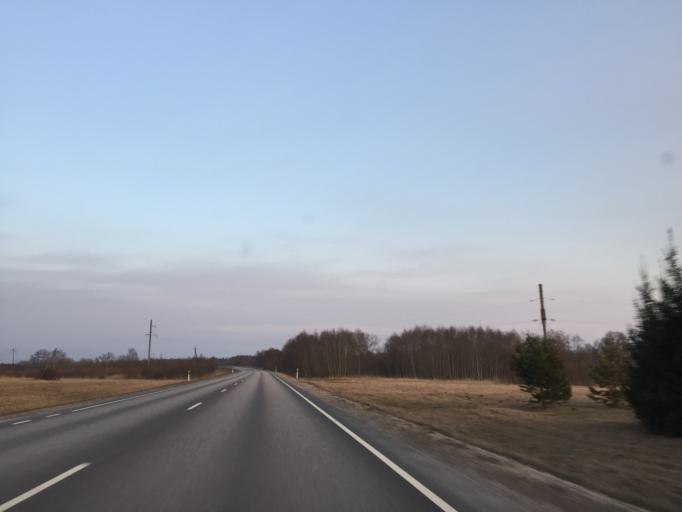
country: EE
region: Paernumaa
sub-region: Audru vald
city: Audru
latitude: 58.4172
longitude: 24.3620
